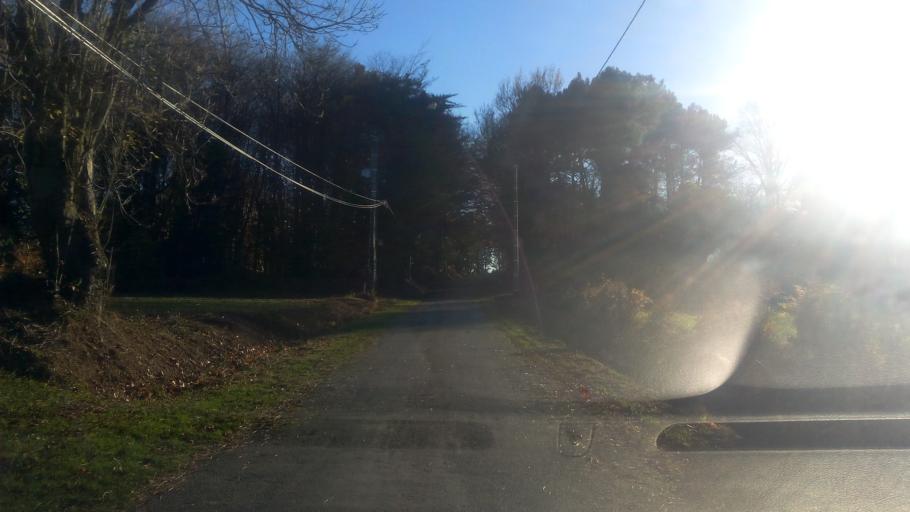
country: FR
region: Brittany
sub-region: Departement du Morbihan
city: Peillac
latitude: 47.7208
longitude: -2.2283
